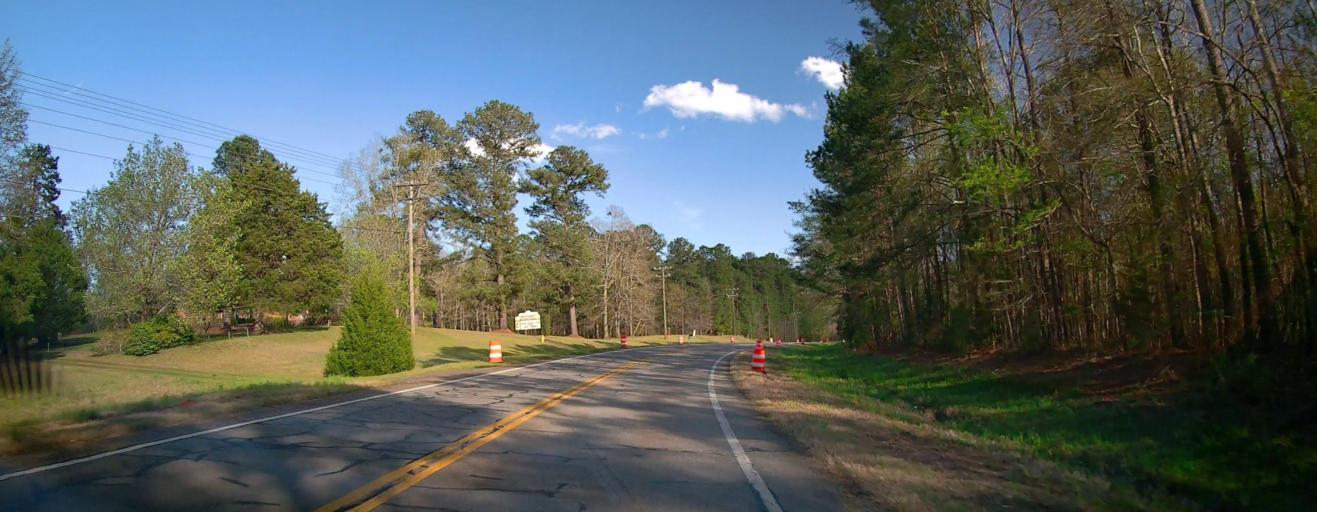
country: US
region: Georgia
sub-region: Baldwin County
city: Milledgeville
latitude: 33.1596
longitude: -83.3544
